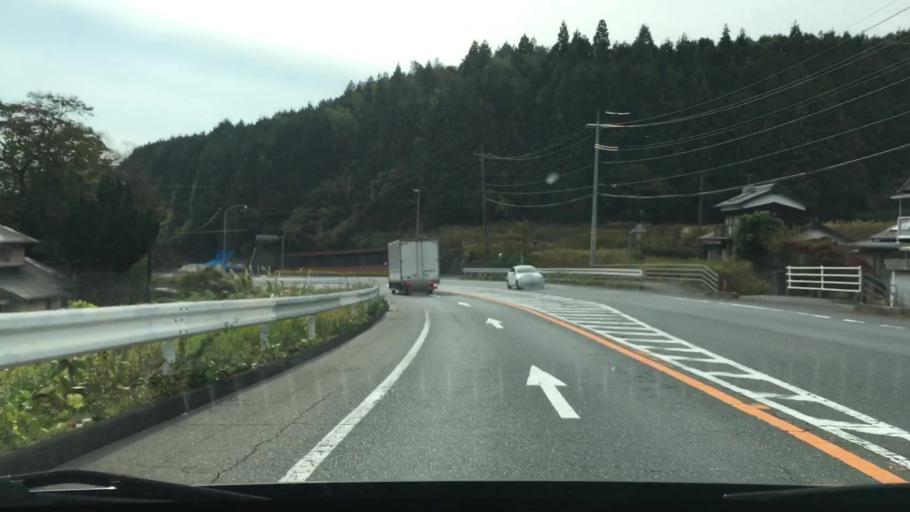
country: JP
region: Yamaguchi
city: Hikari
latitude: 34.0652
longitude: 131.9749
